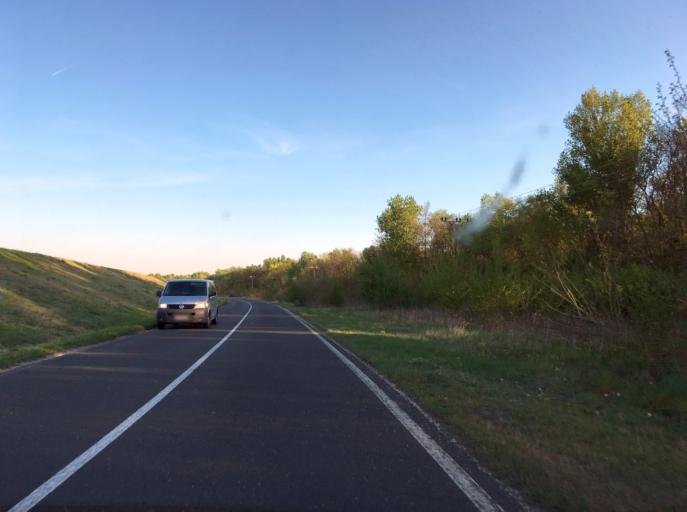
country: HU
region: Gyor-Moson-Sopron
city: Rajka
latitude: 48.0064
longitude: 17.2527
